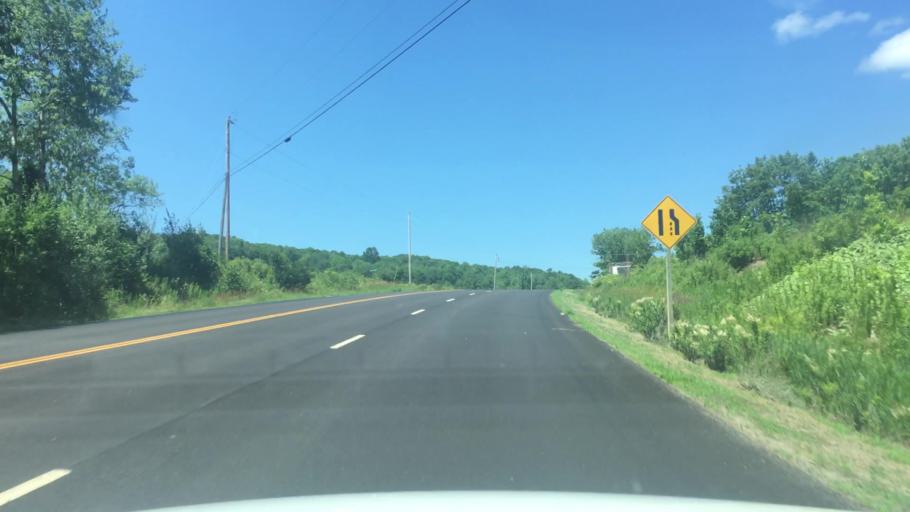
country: US
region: Maine
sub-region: Waldo County
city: Searsmont
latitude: 44.4017
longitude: -69.2958
